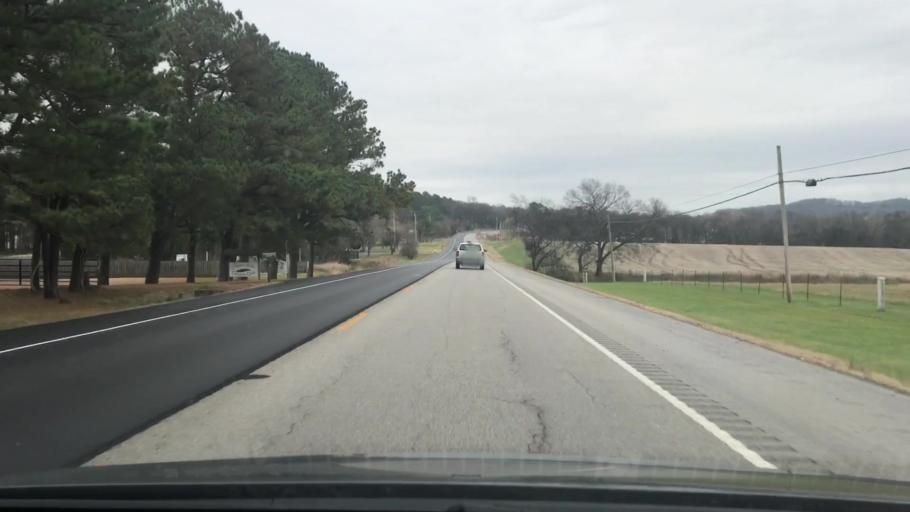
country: US
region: Tennessee
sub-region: Smith County
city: Carthage
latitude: 36.3366
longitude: -86.0284
